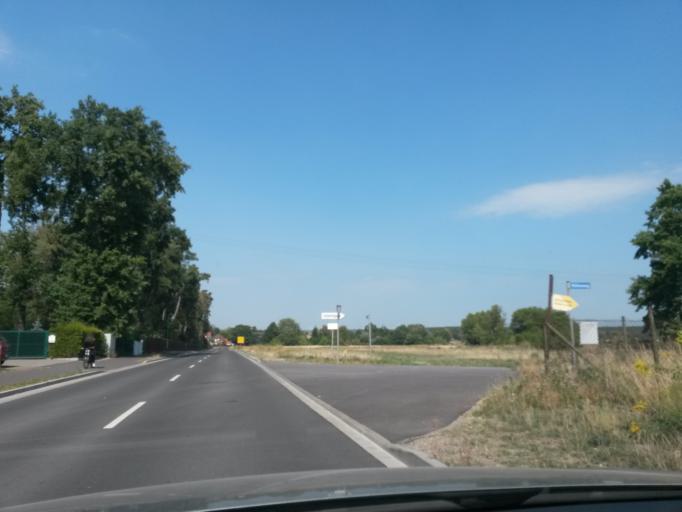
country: DE
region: Saxony-Anhalt
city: Jerichow
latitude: 52.4323
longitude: 11.9973
